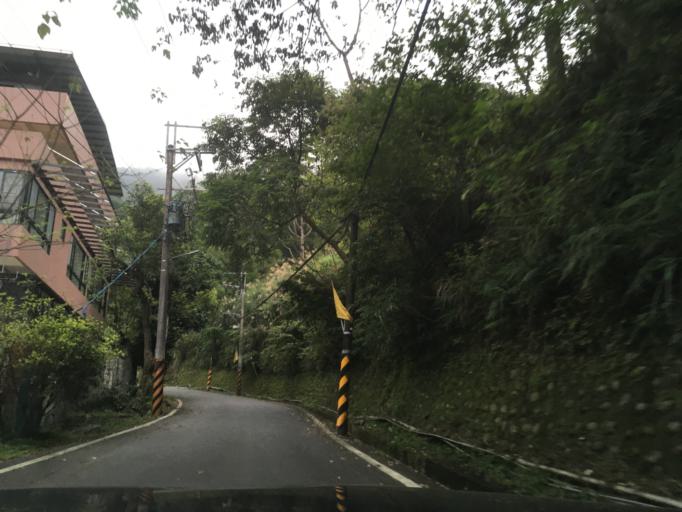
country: TW
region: Taiwan
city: Daxi
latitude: 24.8946
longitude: 121.3785
